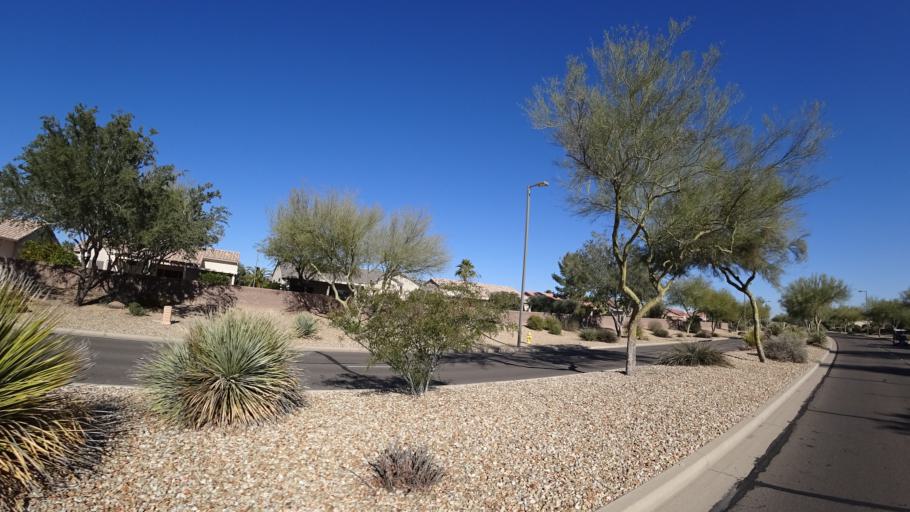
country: US
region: Arizona
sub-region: Maricopa County
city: Sun City West
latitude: 33.6693
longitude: -112.4064
